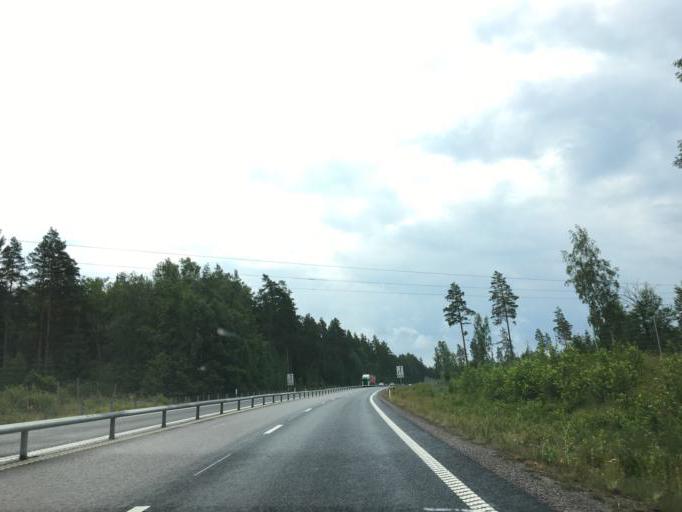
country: SE
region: Soedermanland
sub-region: Katrineholms Kommun
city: Katrineholm
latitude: 58.9005
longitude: 16.2069
